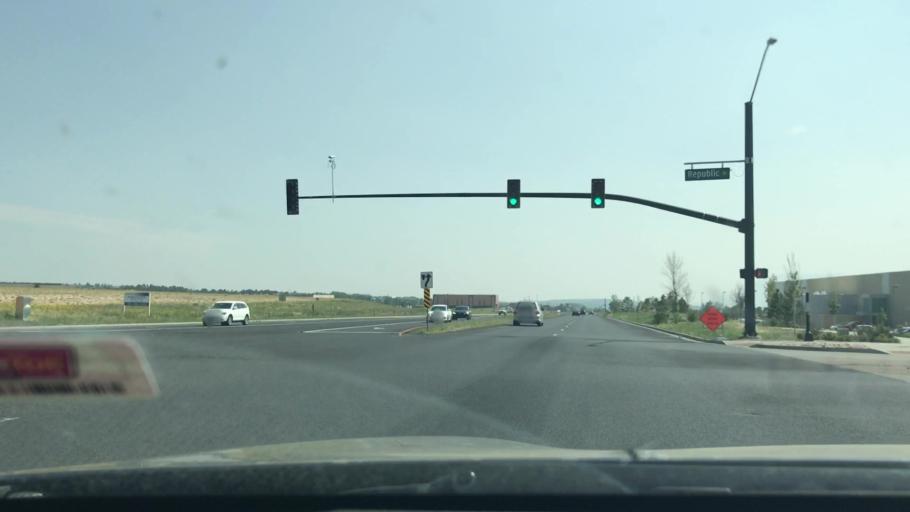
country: US
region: Colorado
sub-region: El Paso County
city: Gleneagle
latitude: 38.9885
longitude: -104.7982
